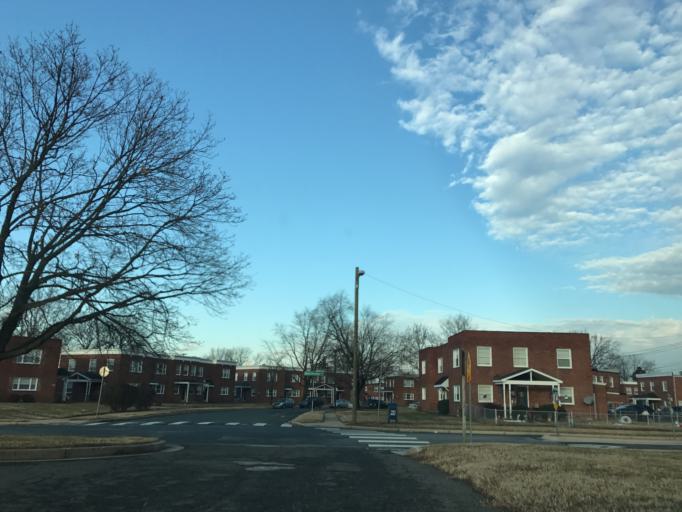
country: US
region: Maryland
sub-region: Baltimore County
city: Dundalk
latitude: 39.2690
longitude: -76.4915
